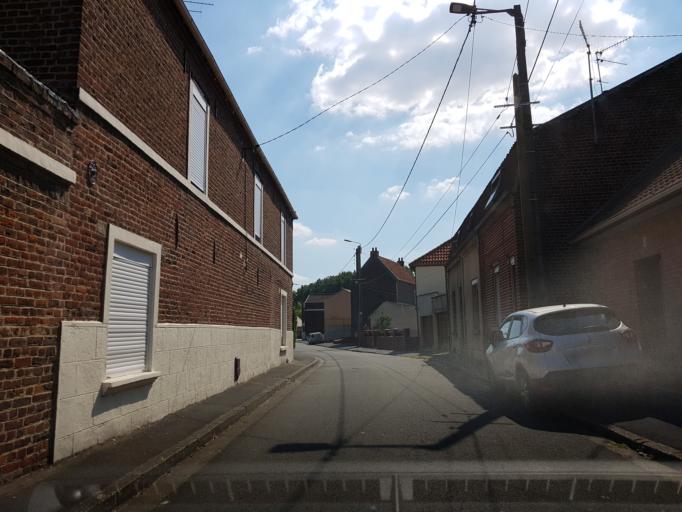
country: FR
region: Nord-Pas-de-Calais
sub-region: Departement du Nord
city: Roeulx
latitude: 50.3042
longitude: 3.3371
